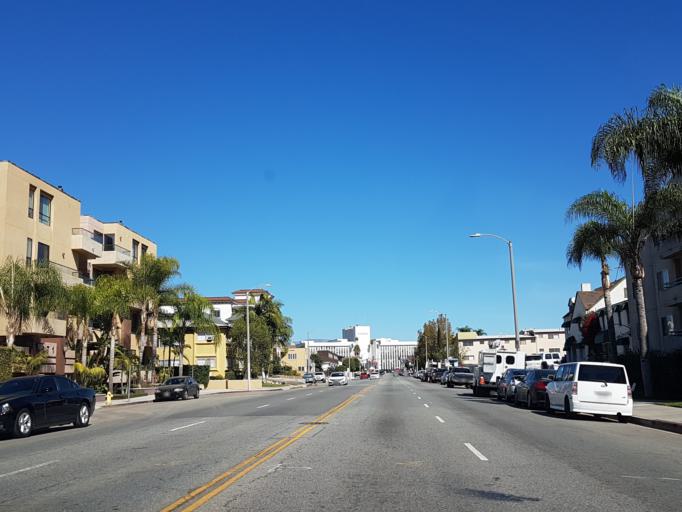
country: US
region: California
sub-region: Los Angeles County
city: Hollywood
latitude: 34.0570
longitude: -118.3217
